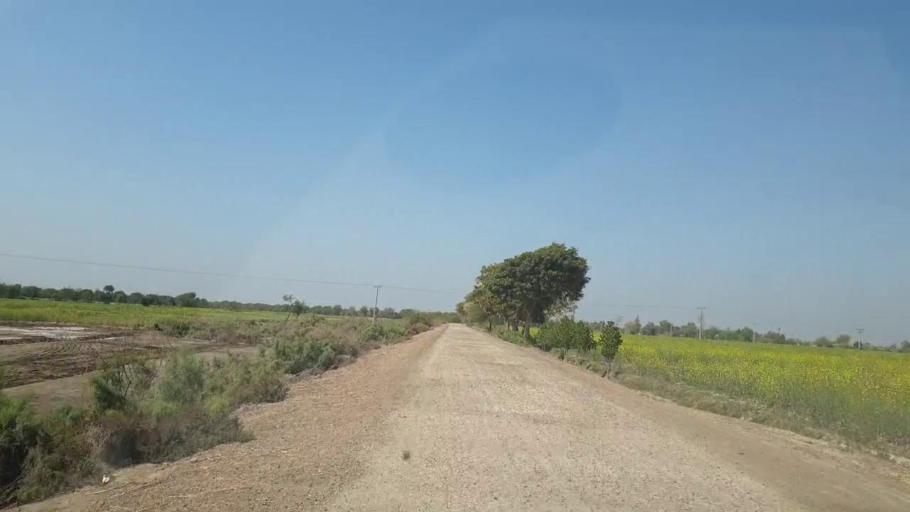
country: PK
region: Sindh
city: Mirpur Khas
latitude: 25.6968
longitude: 69.1020
